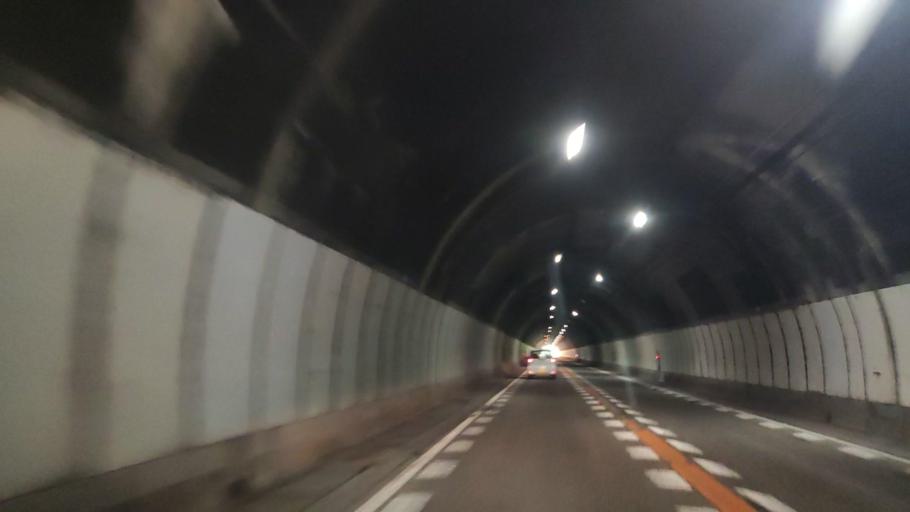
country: JP
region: Hyogo
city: Toyooka
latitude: 35.4839
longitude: 134.5796
